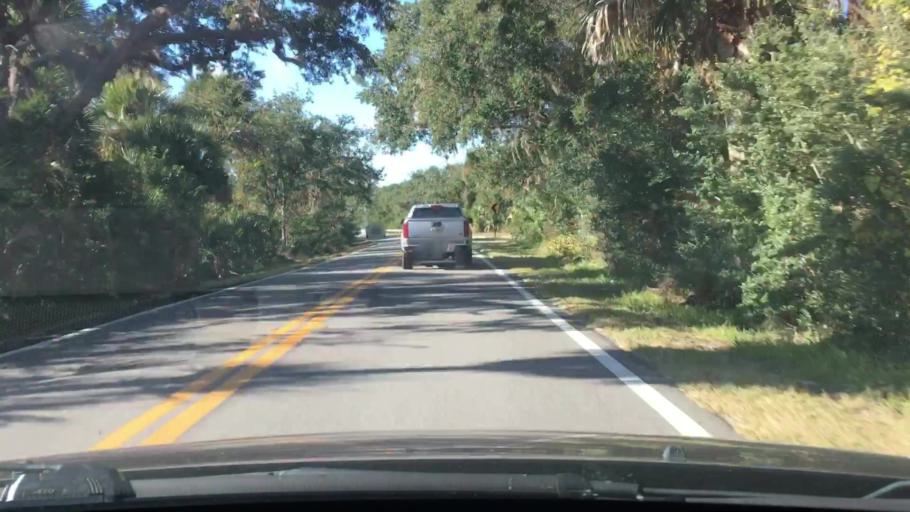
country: US
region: Florida
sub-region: Volusia County
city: Ormond-by-the-Sea
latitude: 29.3527
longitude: -81.1013
